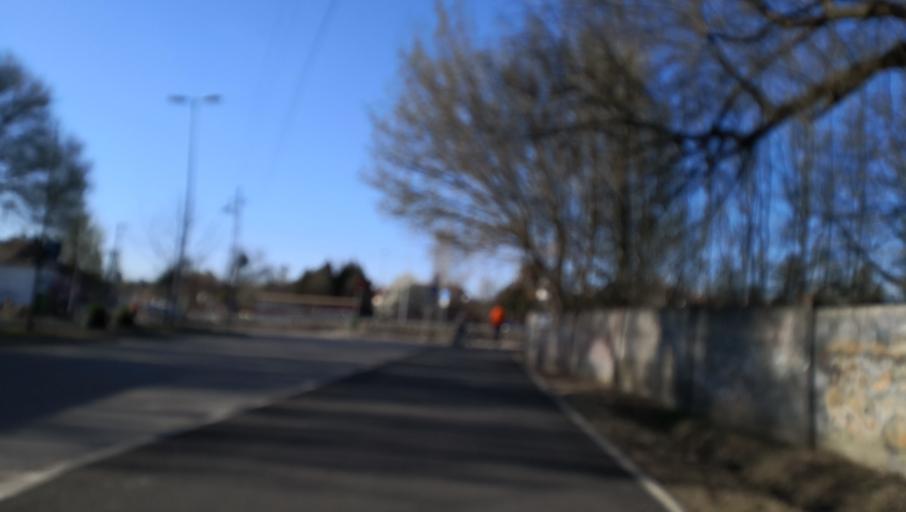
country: HU
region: Budapest
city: Budapest XVII. keruelet
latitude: 47.4909
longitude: 19.2830
